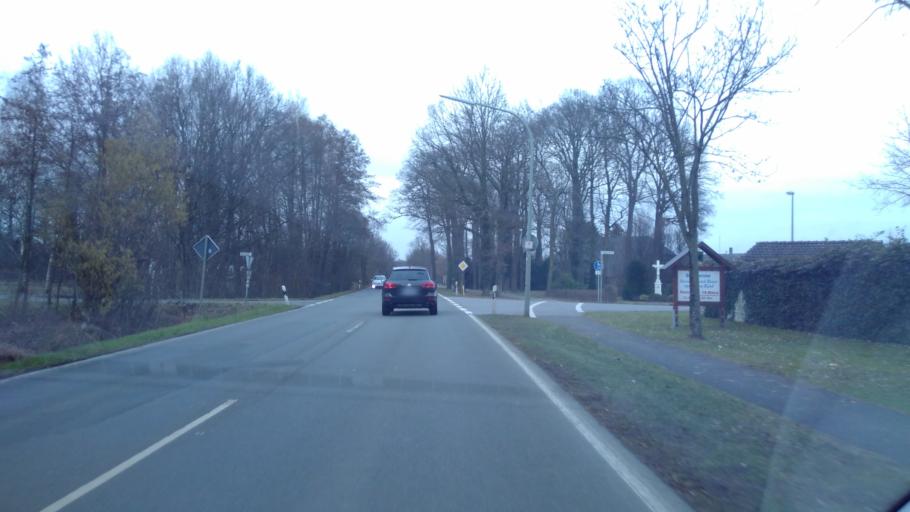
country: DE
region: North Rhine-Westphalia
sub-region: Regierungsbezirk Detmold
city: Delbruck
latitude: 51.8186
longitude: 8.5579
